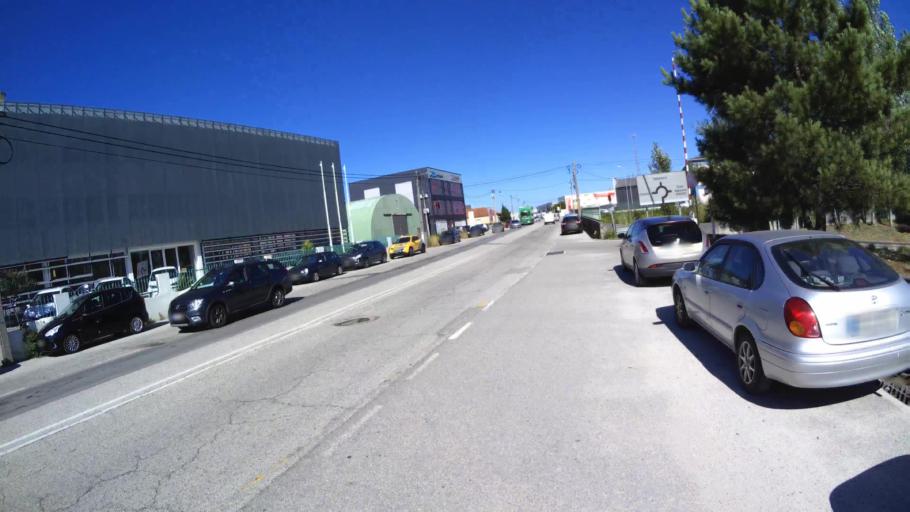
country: PT
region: Aveiro
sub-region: Aveiro
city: Aveiro
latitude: 40.6518
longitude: -8.6130
